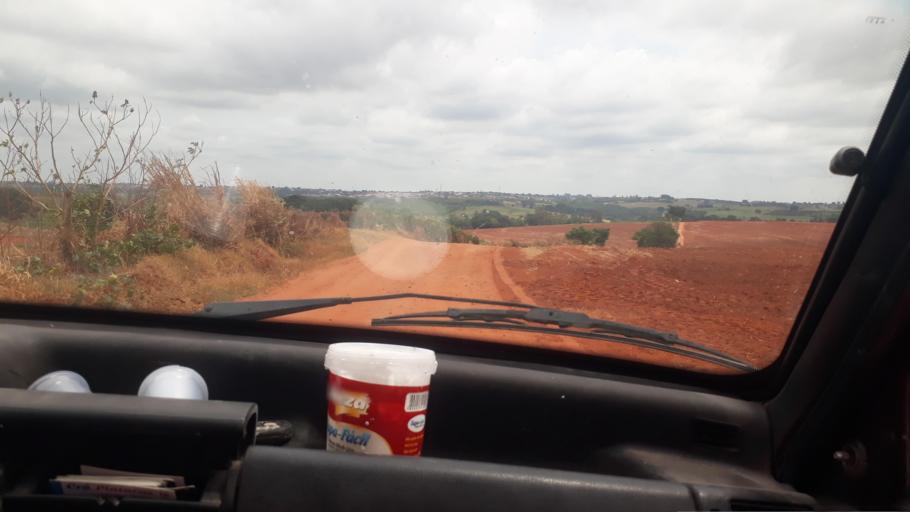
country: BR
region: Sao Paulo
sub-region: Regente Feijo
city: Regente Feijo
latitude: -22.2603
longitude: -51.3019
